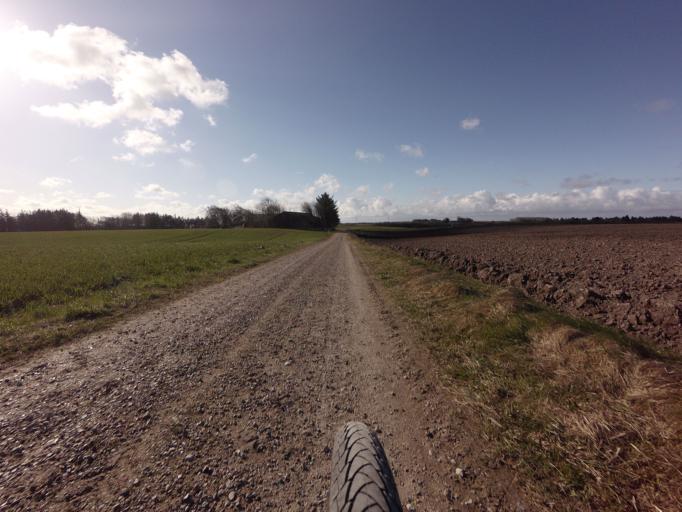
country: DK
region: North Denmark
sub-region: Hjorring Kommune
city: Vra
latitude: 57.3618
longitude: 9.8170
